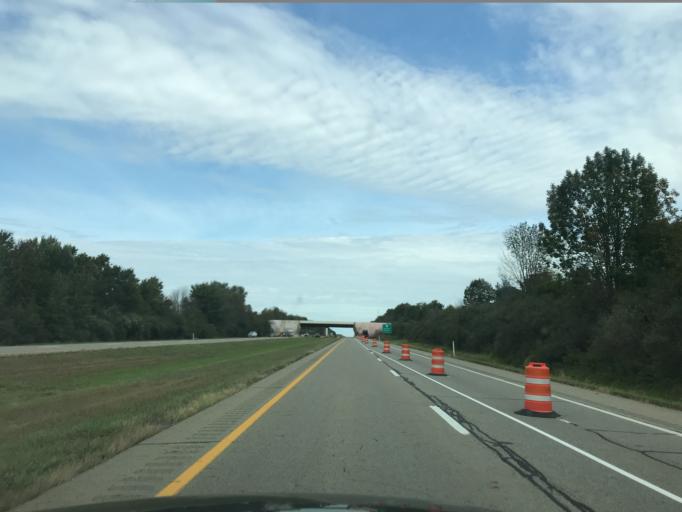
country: US
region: Ohio
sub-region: Ashtabula County
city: Roaming Shores
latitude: 41.5882
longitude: -80.7133
